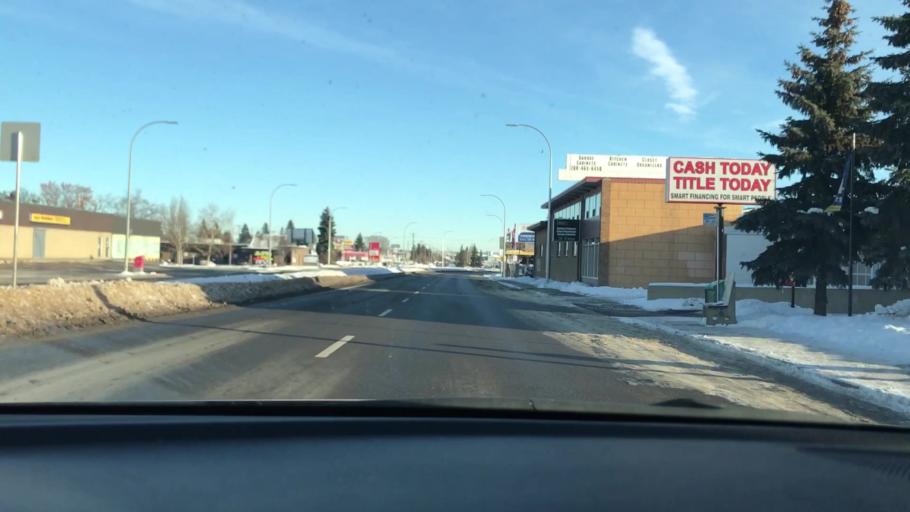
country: CA
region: Alberta
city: Edmonton
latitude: 53.5180
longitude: -113.4419
